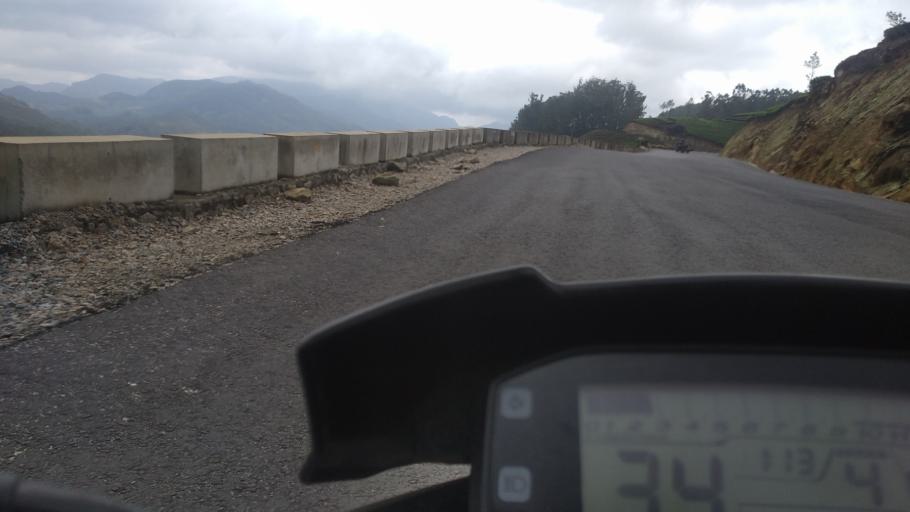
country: IN
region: Kerala
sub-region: Idukki
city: Munnar
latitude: 10.0802
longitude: 77.0827
